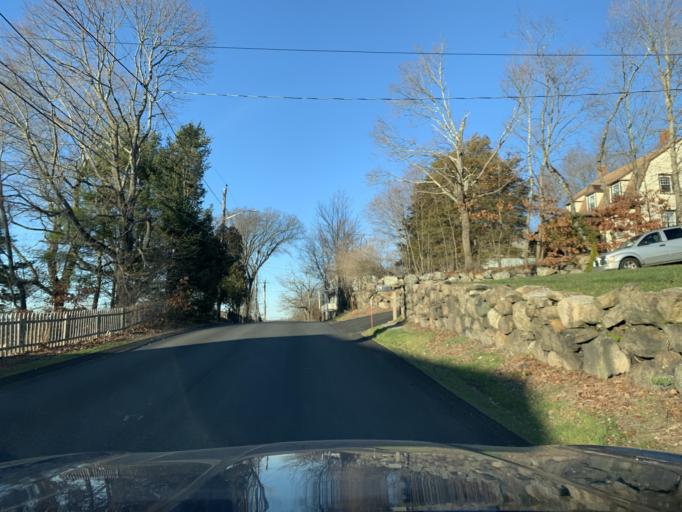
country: US
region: Rhode Island
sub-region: Kent County
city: West Warwick
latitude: 41.6883
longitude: -71.5202
